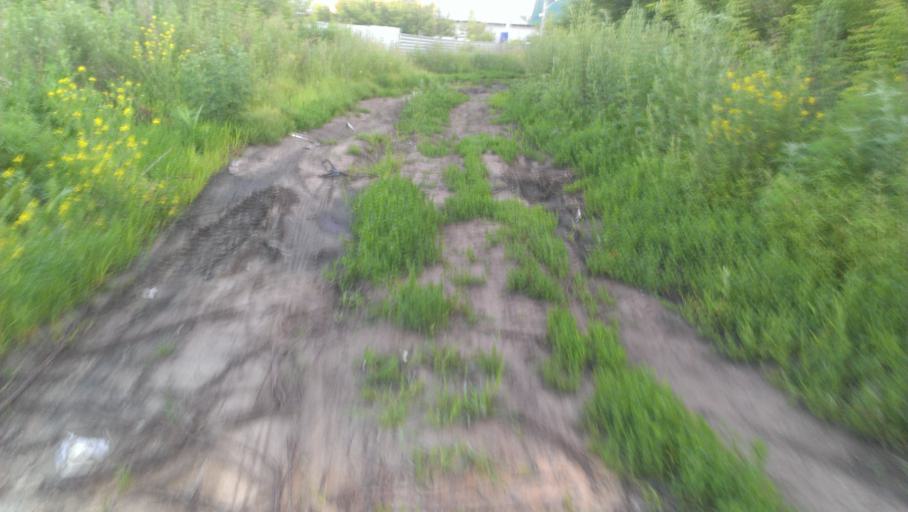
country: RU
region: Altai Krai
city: Novosilikatnyy
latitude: 53.3643
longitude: 83.6499
